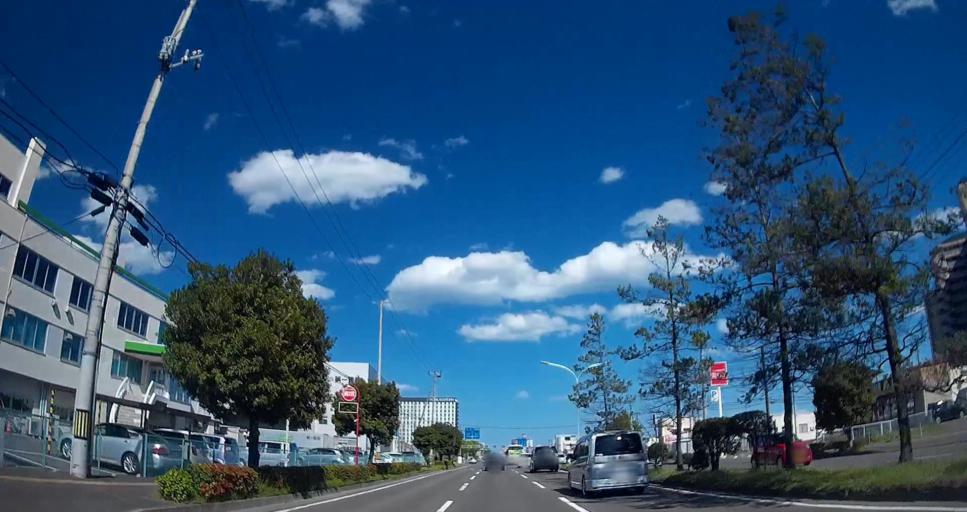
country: JP
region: Miyagi
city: Sendai-shi
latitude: 38.2515
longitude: 140.9253
